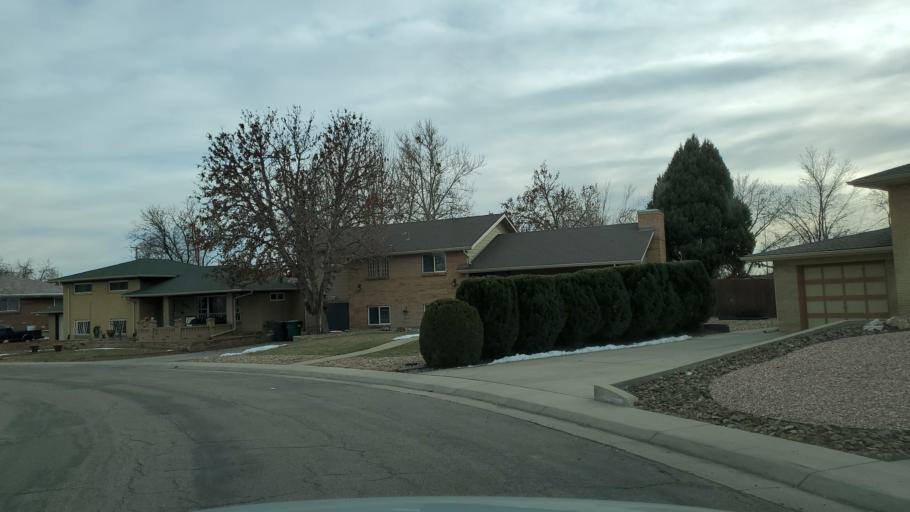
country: US
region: Colorado
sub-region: Adams County
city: Westminster
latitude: 39.8397
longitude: -105.0235
